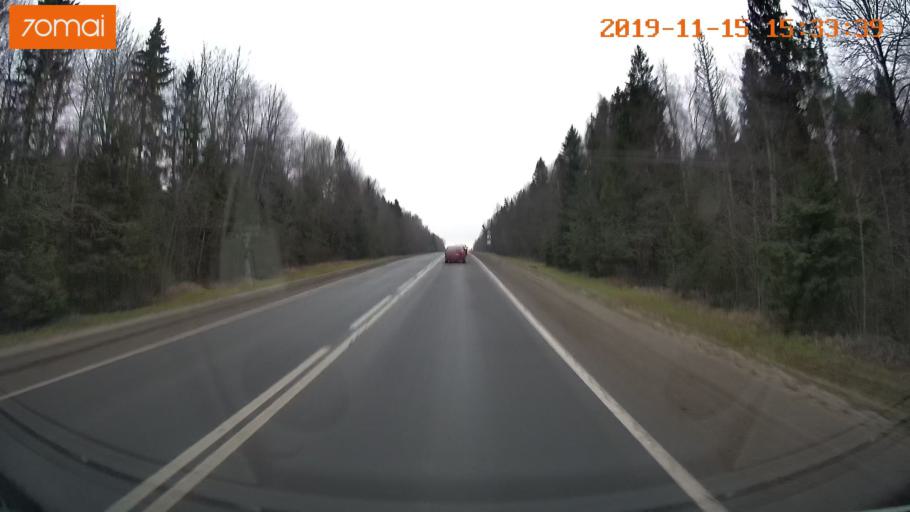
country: RU
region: Jaroslavl
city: Danilov
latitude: 58.0782
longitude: 40.0919
